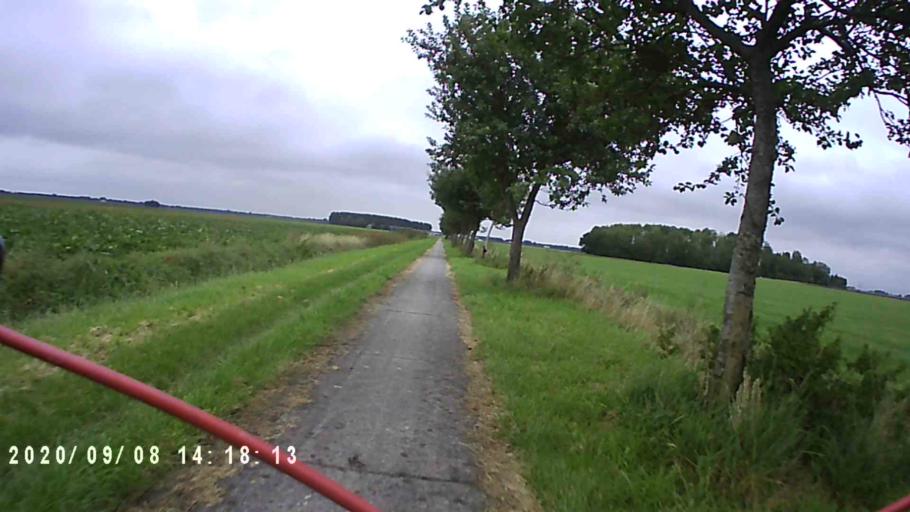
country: NL
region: Groningen
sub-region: Gemeente Slochteren
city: Slochteren
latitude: 53.2075
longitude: 6.8373
